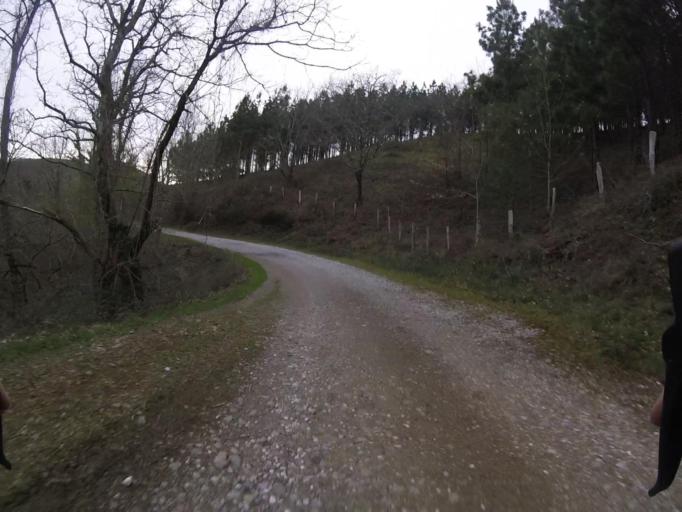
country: ES
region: Navarre
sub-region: Provincia de Navarra
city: Lesaka
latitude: 43.2785
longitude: -1.7491
